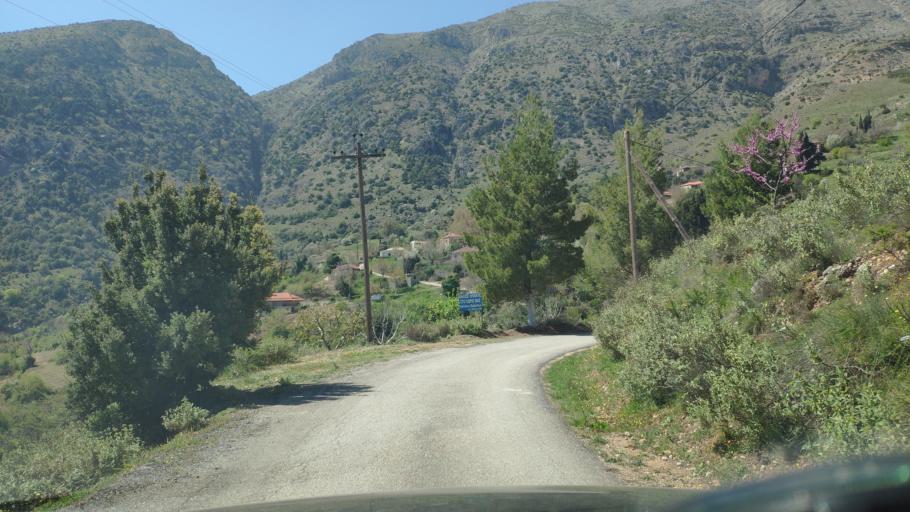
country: GR
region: West Greece
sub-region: Nomos Achaias
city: Akrata
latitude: 38.0728
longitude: 22.3180
